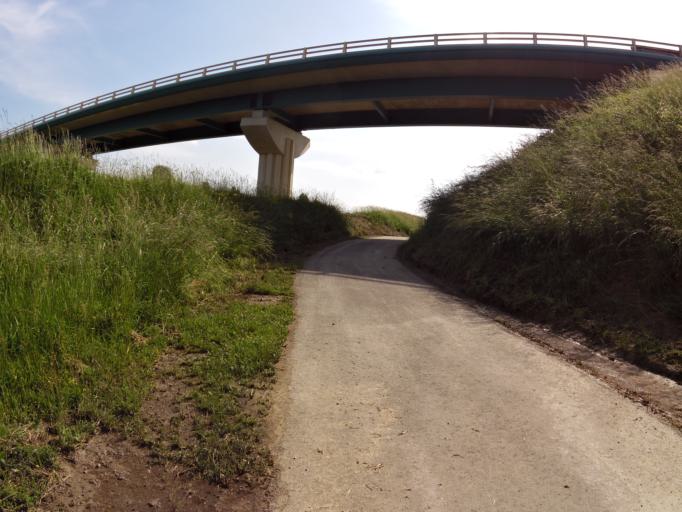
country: FR
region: Champagne-Ardenne
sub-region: Departement de l'Aube
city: Saint-Julien-les-Villas
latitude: 48.2650
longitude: 4.1162
